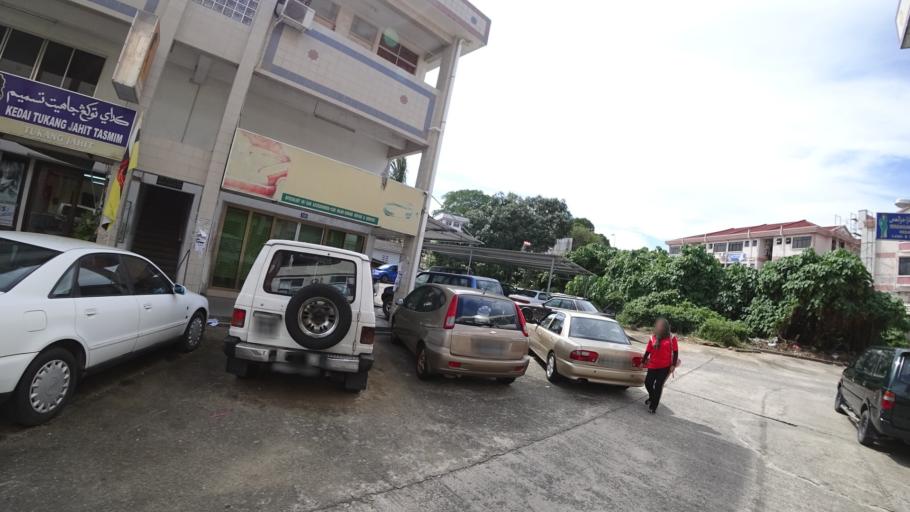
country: BN
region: Brunei and Muara
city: Bandar Seri Begawan
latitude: 4.8875
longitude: 114.8391
